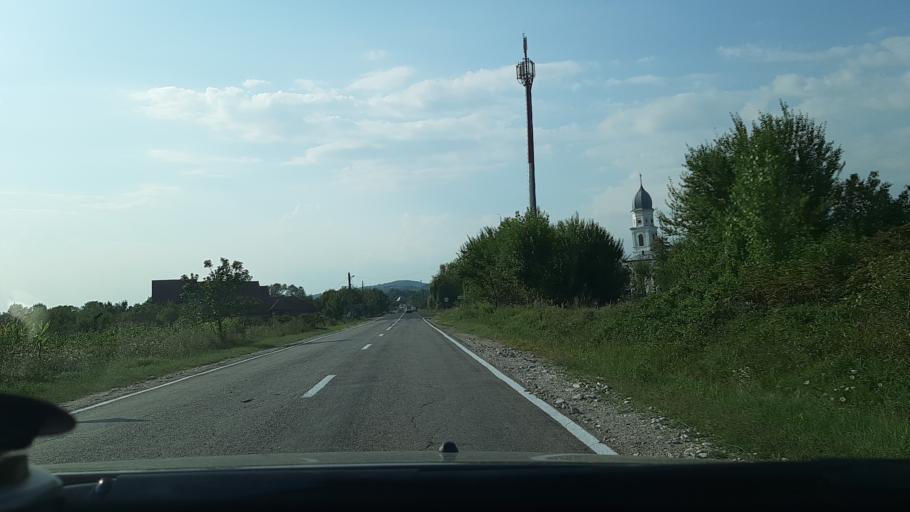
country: RO
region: Gorj
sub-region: Comuna Scoarta
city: Scoarta
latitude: 45.0152
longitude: 23.4696
